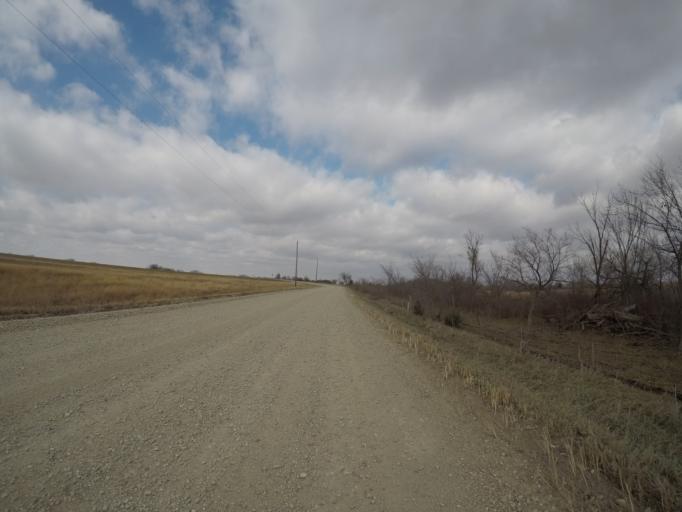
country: US
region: Kansas
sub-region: Wabaunsee County
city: Alma
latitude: 38.8557
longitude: -96.3727
